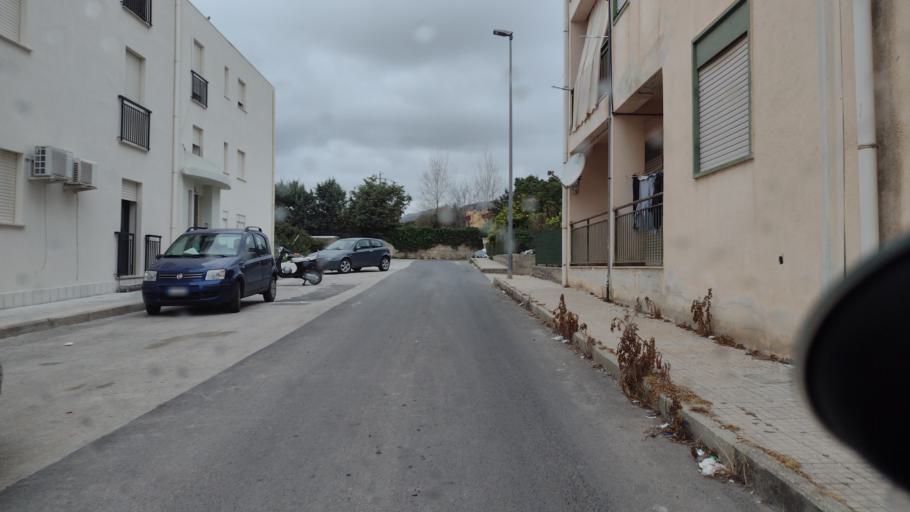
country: IT
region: Sicily
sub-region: Provincia di Siracusa
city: Avola
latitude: 36.9192
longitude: 15.1402
